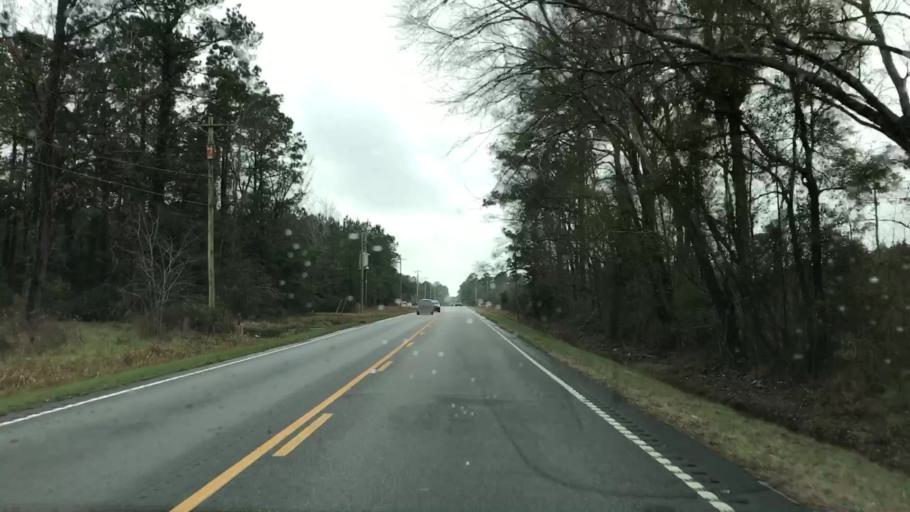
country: US
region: South Carolina
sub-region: Horry County
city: Socastee
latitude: 33.7392
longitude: -79.0810
